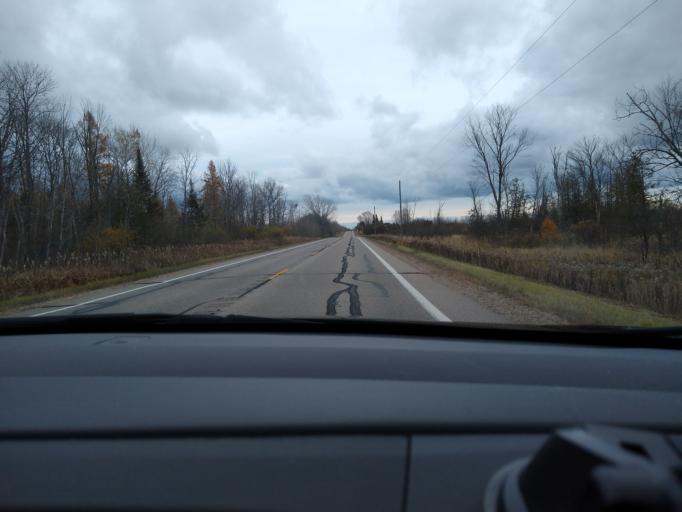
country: US
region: Michigan
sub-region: Delta County
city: Escanaba
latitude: 45.7728
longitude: -87.3152
